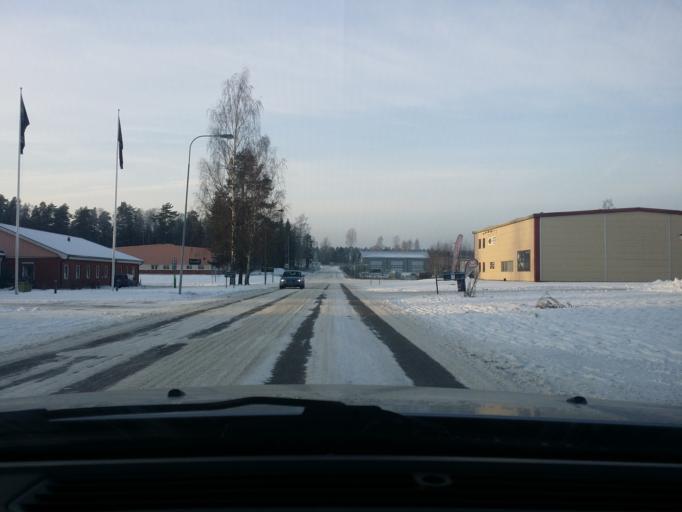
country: SE
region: OErebro
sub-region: Lindesbergs Kommun
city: Lindesberg
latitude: 59.5994
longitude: 15.2021
